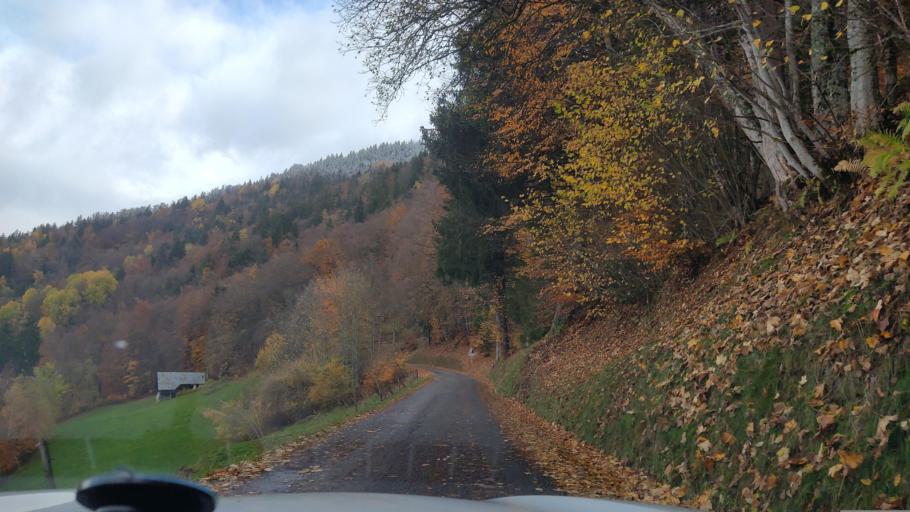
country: FR
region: Rhone-Alpes
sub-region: Departement de la Savoie
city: Albertville
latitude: 45.6809
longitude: 6.4225
